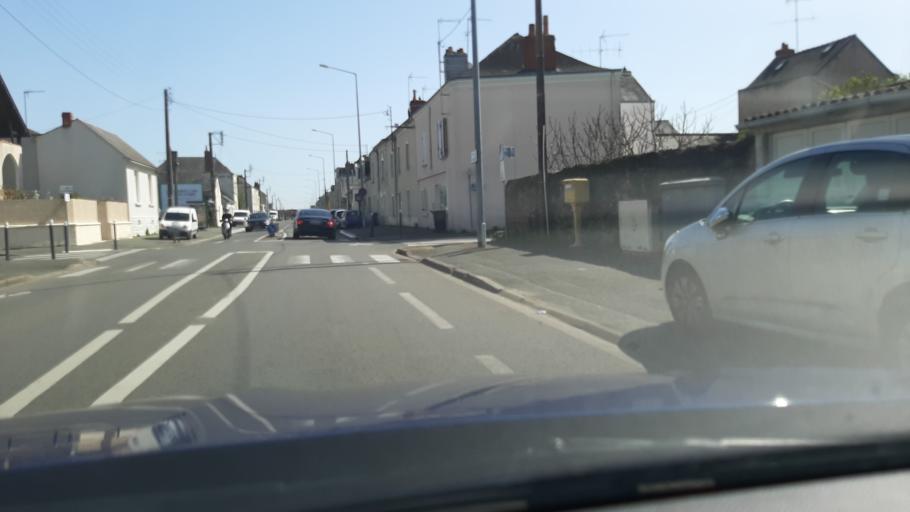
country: FR
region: Pays de la Loire
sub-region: Departement de Maine-et-Loire
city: Les Ponts-de-Ce
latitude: 47.4514
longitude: -0.5206
